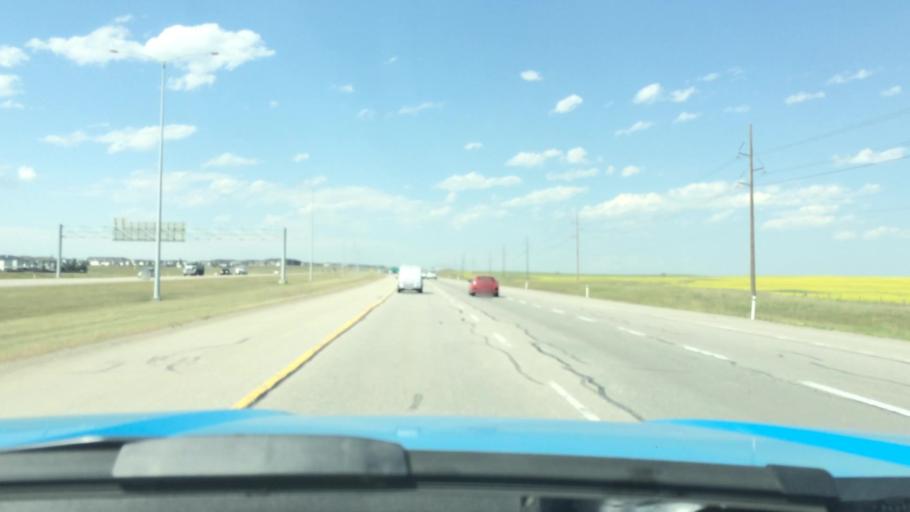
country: CA
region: Alberta
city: Chestermere
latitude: 51.1030
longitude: -113.9185
